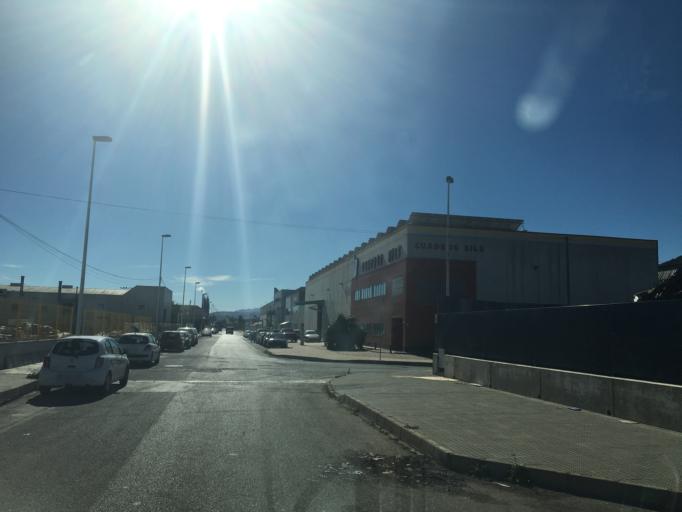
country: ES
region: Murcia
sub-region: Murcia
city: Santomera
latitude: 38.0744
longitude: -1.0588
